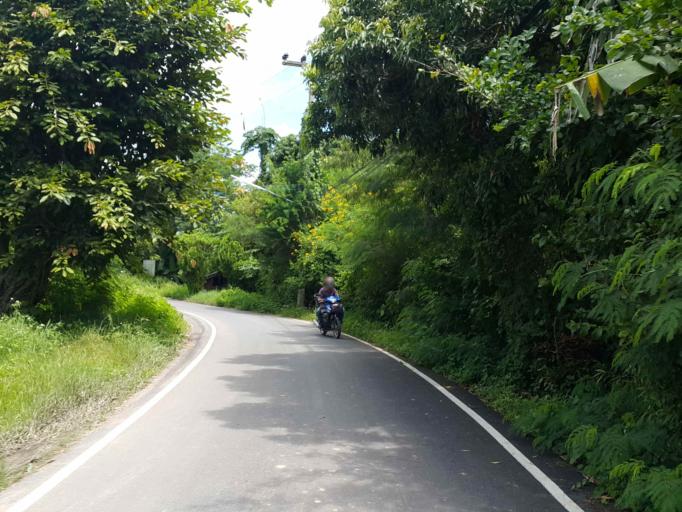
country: TH
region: Chiang Mai
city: San Sai
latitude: 18.8078
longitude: 99.0473
